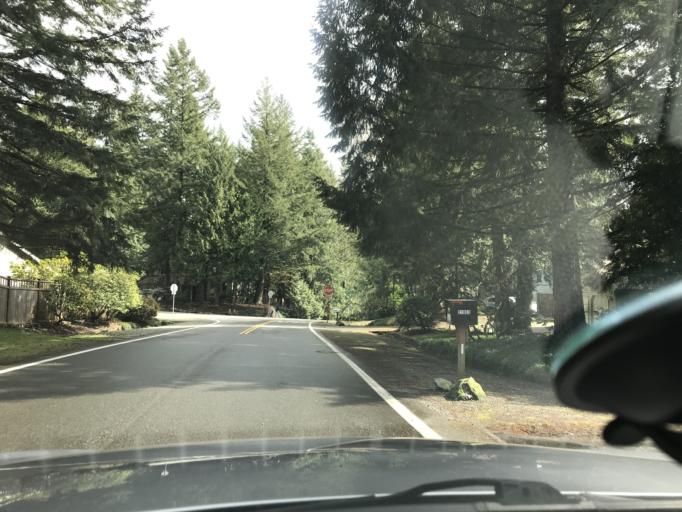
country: US
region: Washington
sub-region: King County
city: City of Sammamish
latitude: 47.5794
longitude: -122.0483
